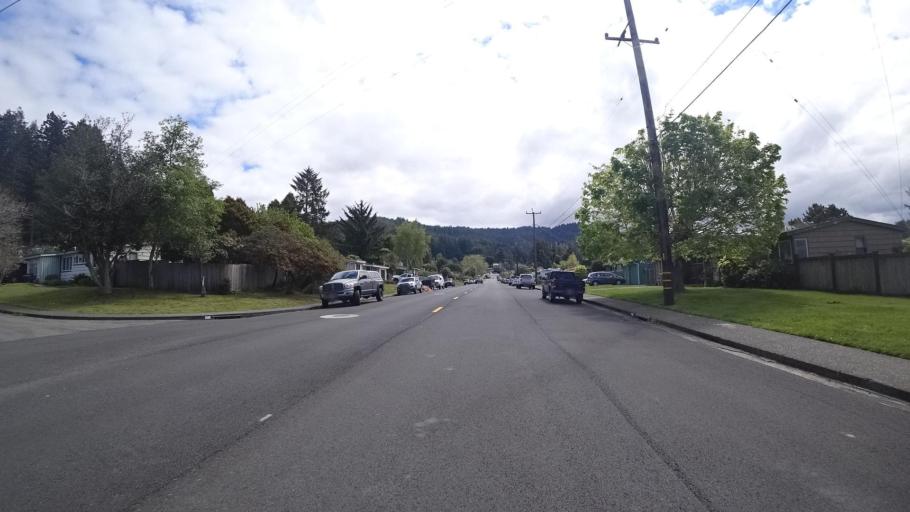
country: US
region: California
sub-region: Humboldt County
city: Bayside
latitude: 40.8585
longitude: -124.0676
